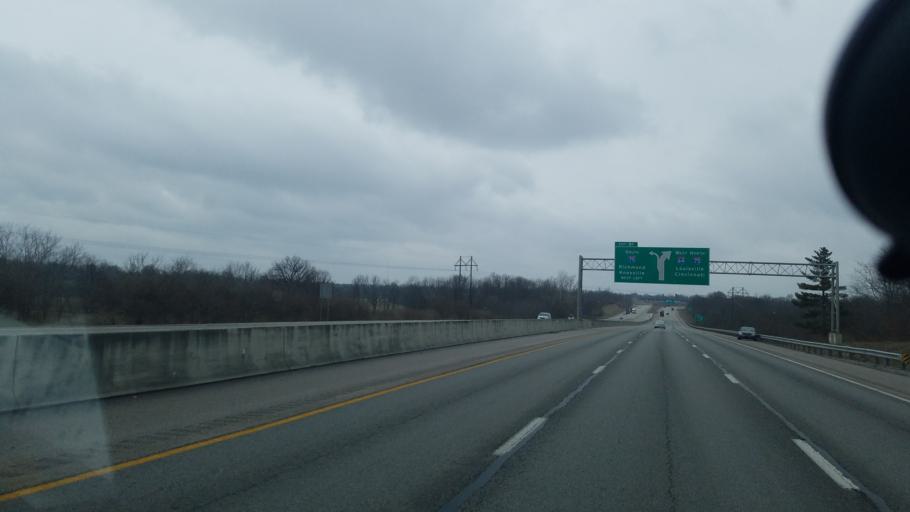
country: US
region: Kentucky
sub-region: Fayette County
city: Lexington-Fayette
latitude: 38.0593
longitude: -84.4102
